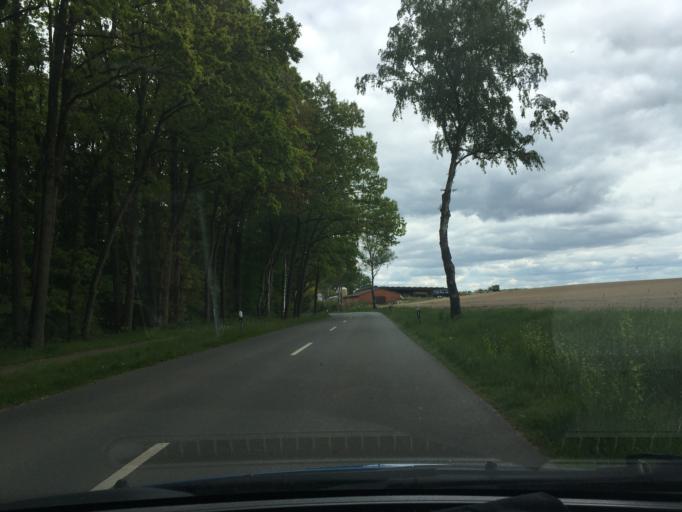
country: DE
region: Lower Saxony
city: Suderburg
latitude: 52.8629
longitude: 10.4225
